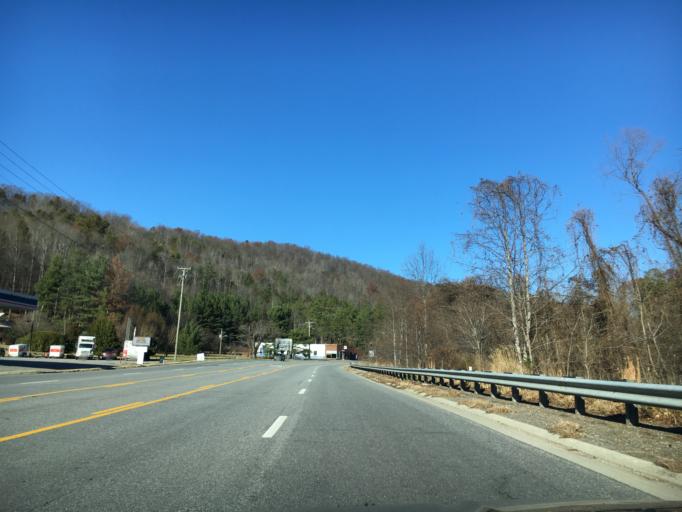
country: US
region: Virginia
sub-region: Patrick County
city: Stuart
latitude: 36.6530
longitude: -80.2834
